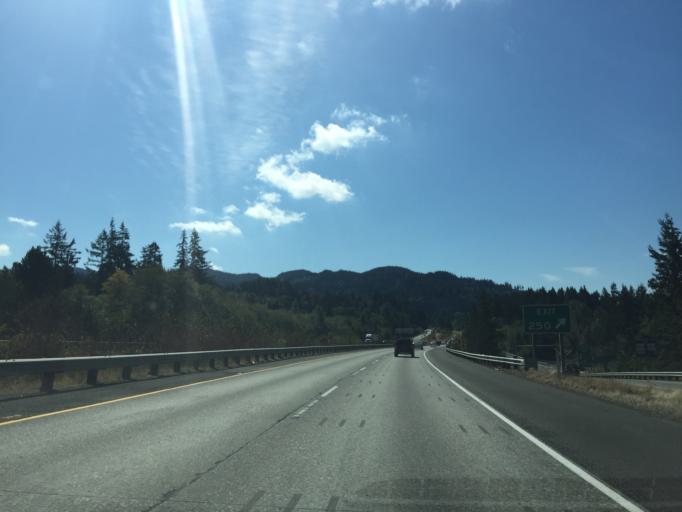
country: US
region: Washington
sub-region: Whatcom County
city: Bellingham
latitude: 48.7162
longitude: -122.4741
